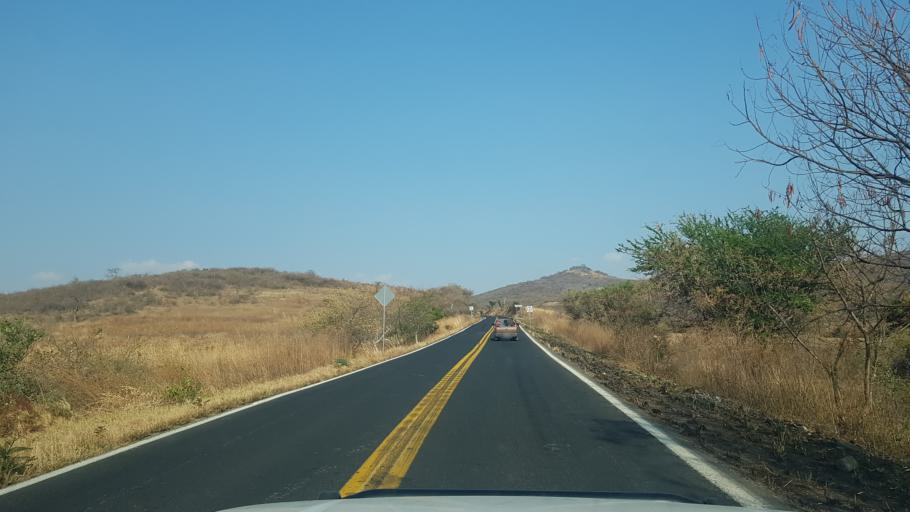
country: MX
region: Puebla
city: Calmeca
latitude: 18.6420
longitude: -98.6148
